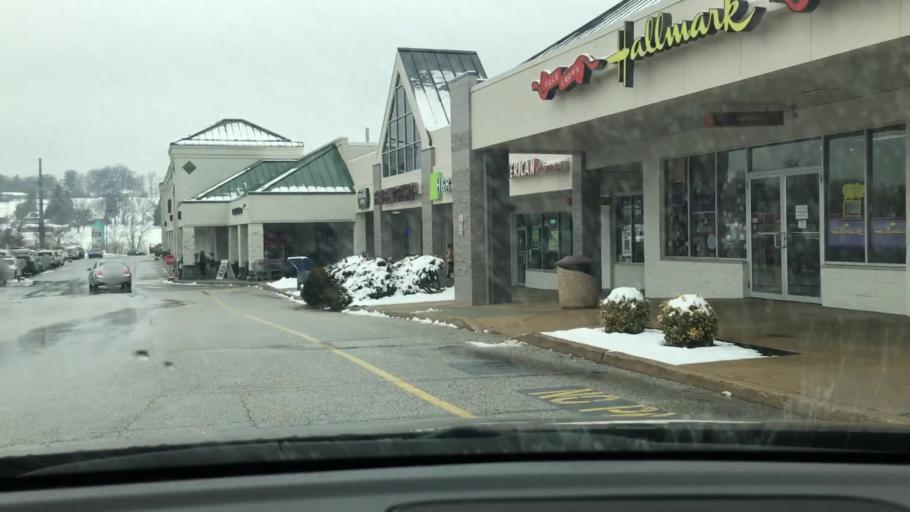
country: US
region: Pennsylvania
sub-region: York County
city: Spry
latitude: 39.9334
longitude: -76.6819
